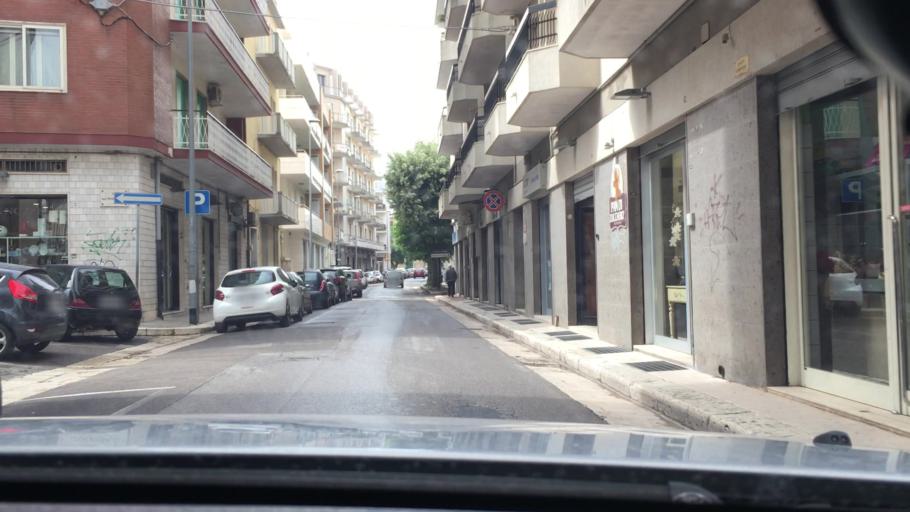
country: IT
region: Apulia
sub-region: Provincia di Bari
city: Gioia del Colle
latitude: 40.7965
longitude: 16.9199
